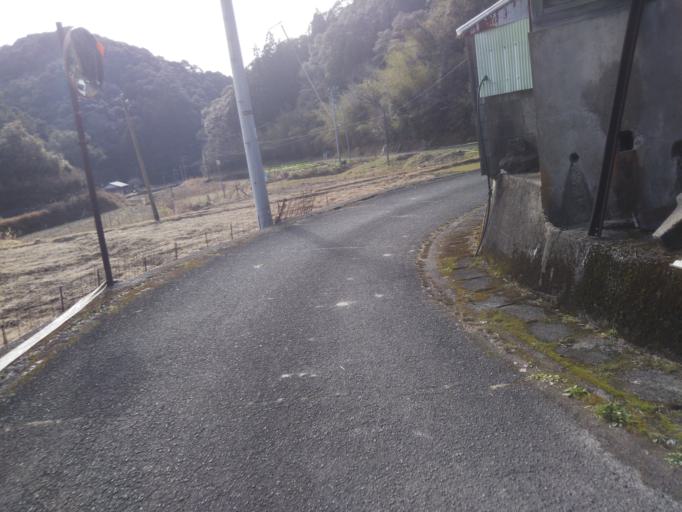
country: JP
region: Kochi
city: Nakamura
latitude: 33.0460
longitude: 132.9877
